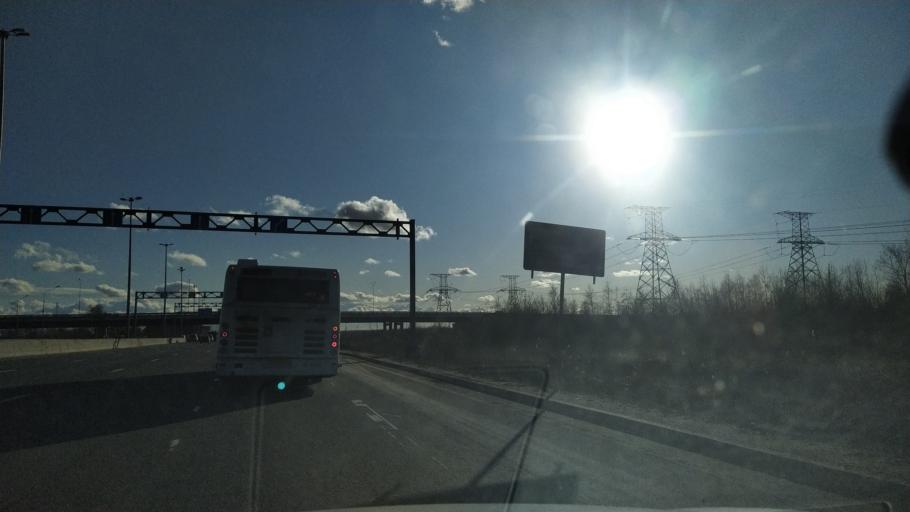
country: RU
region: St.-Petersburg
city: Aleksandrovskaya
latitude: 59.7202
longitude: 30.2841
